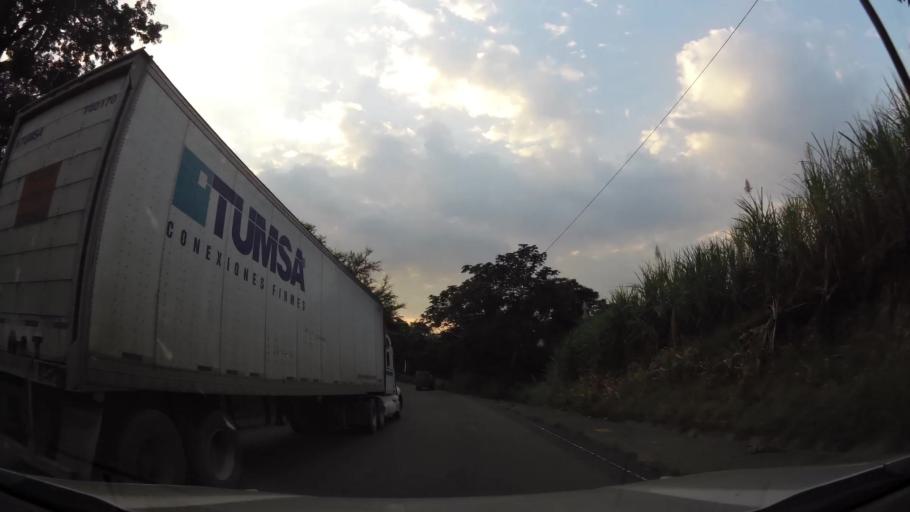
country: GT
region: Escuintla
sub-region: Municipio de La Democracia
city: La Democracia
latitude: 14.2674
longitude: -90.8881
